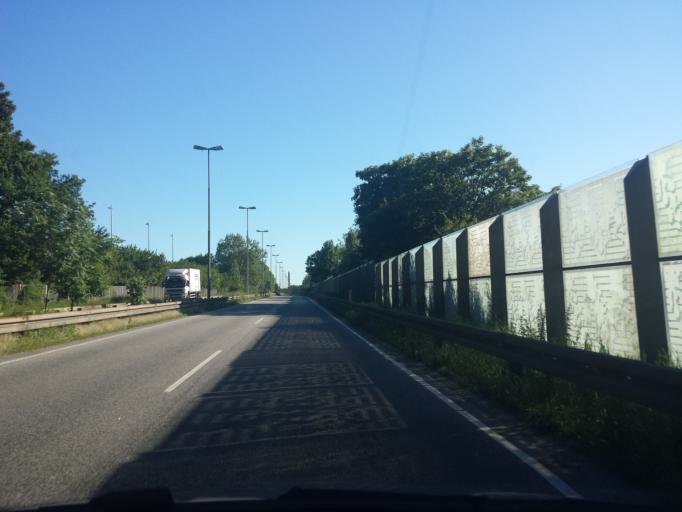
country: DK
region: Capital Region
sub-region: Ballerup Kommune
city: Ballerup
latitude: 55.7278
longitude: 12.3711
